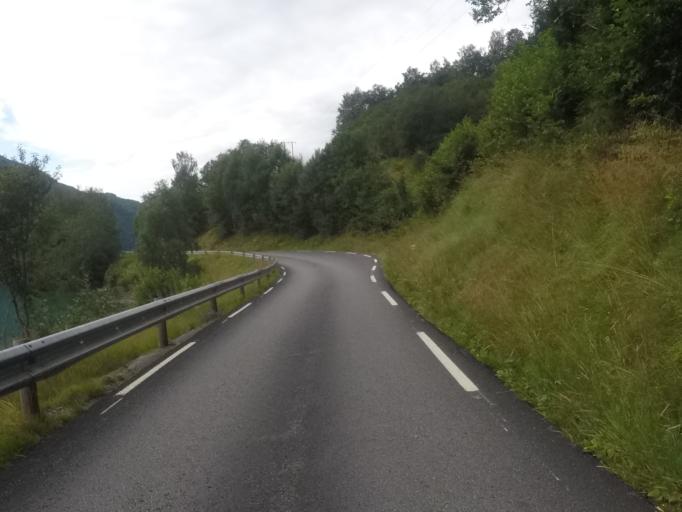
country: NO
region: Sogn og Fjordane
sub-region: Stryn
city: Stryn
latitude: 61.8462
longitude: 6.9330
